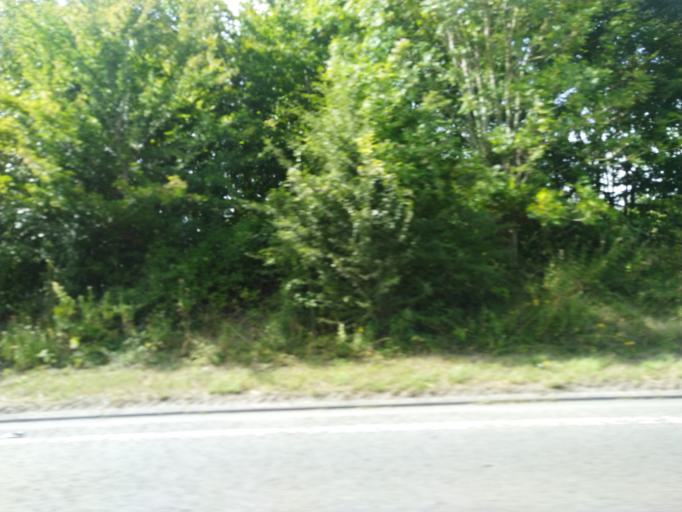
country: GB
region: England
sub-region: Dorset
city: Blandford Forum
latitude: 50.8589
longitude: -2.1495
